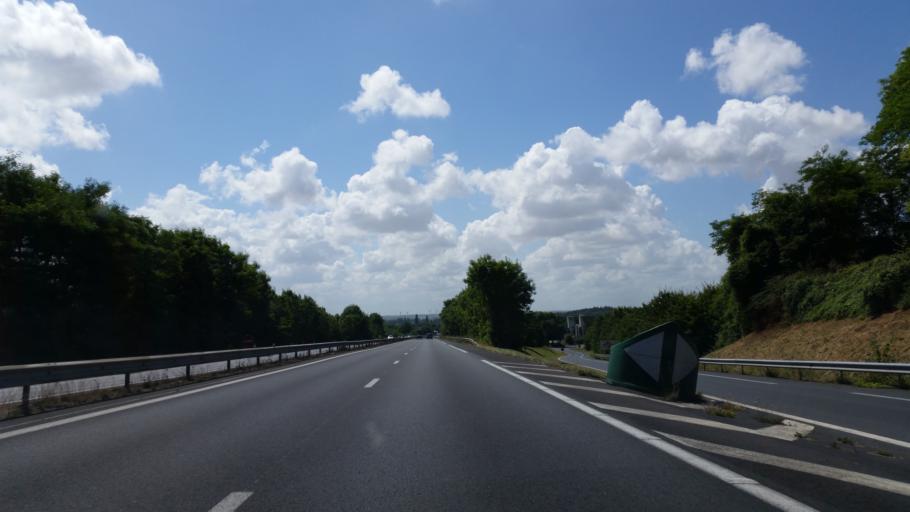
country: FR
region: Lower Normandy
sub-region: Departement du Calvados
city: Troarn
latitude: 49.1814
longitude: -0.1990
